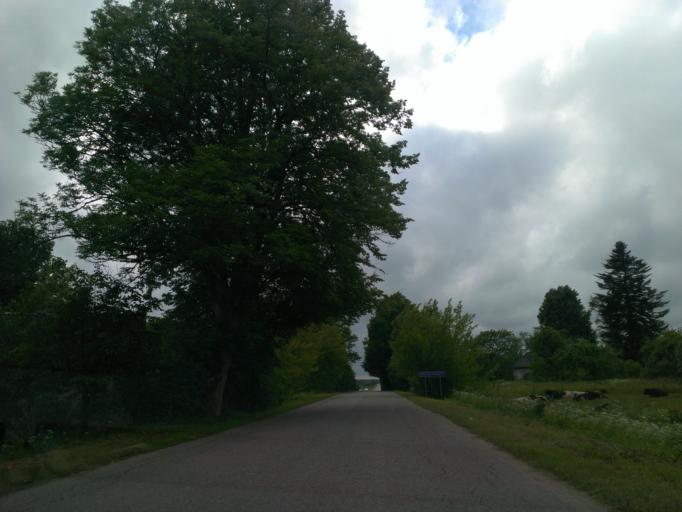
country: LV
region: Aizpute
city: Aizpute
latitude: 56.7128
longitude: 21.4767
